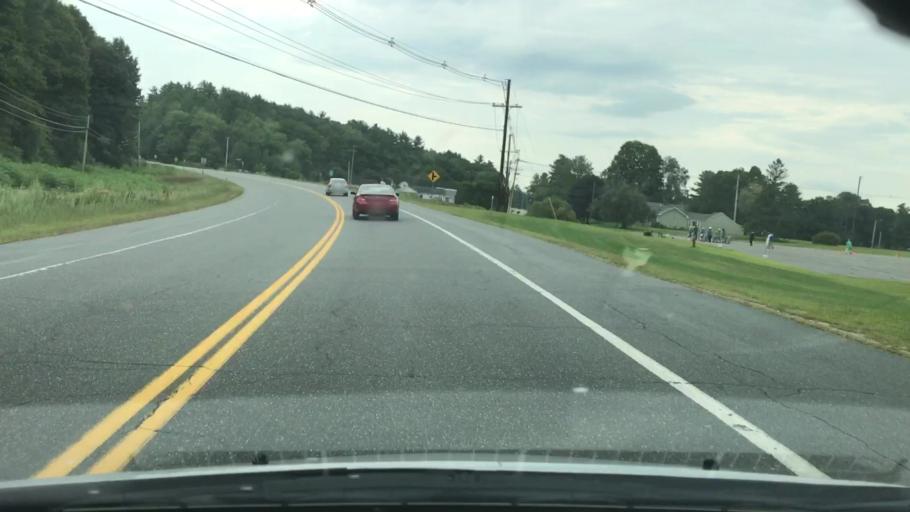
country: US
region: New Hampshire
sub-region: Grafton County
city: North Haverhill
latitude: 44.1133
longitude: -72.0406
